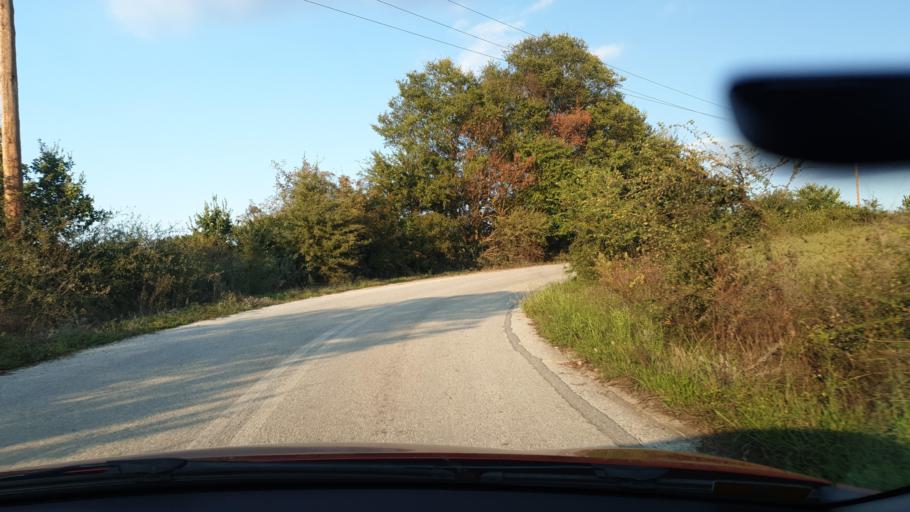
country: GR
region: Central Macedonia
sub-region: Nomos Thessalonikis
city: Nea Apollonia
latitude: 40.5554
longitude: 23.4317
